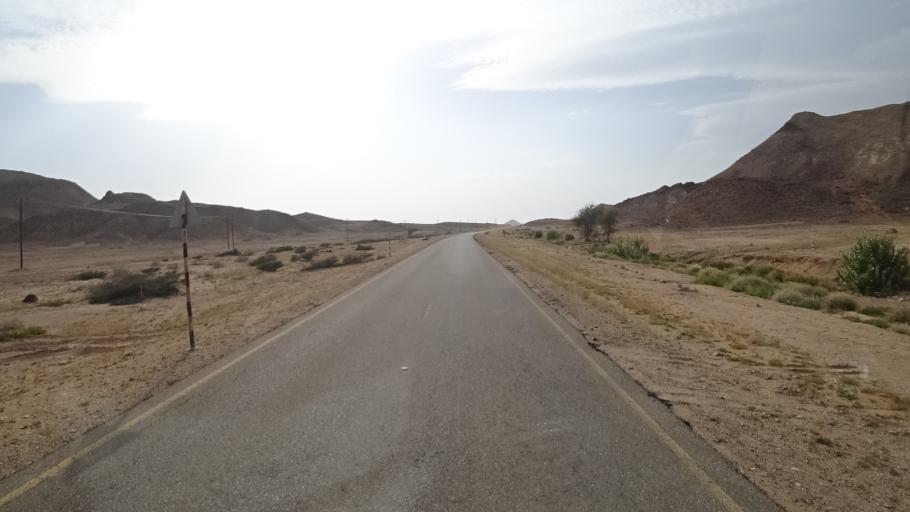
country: OM
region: Ash Sharqiyah
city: Sur
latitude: 22.4345
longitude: 59.8113
